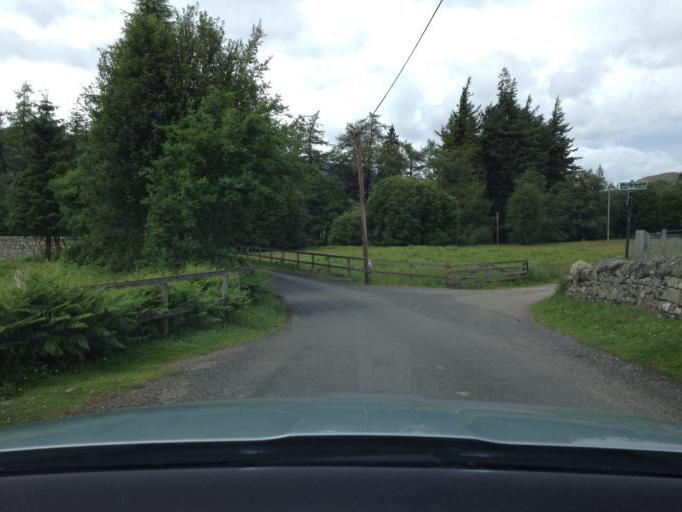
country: GB
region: Scotland
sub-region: Aberdeenshire
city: Ballater
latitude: 56.9115
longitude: -2.9137
